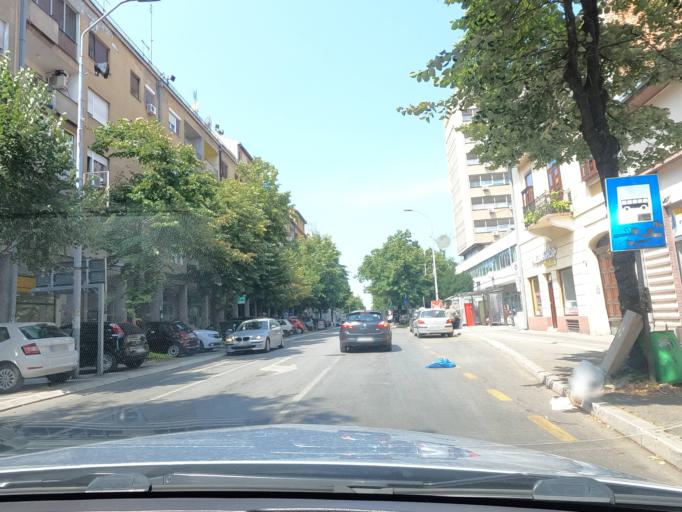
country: RS
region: Autonomna Pokrajina Vojvodina
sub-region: Juznobanatski Okrug
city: Pancevo
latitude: 44.8695
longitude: 20.6401
